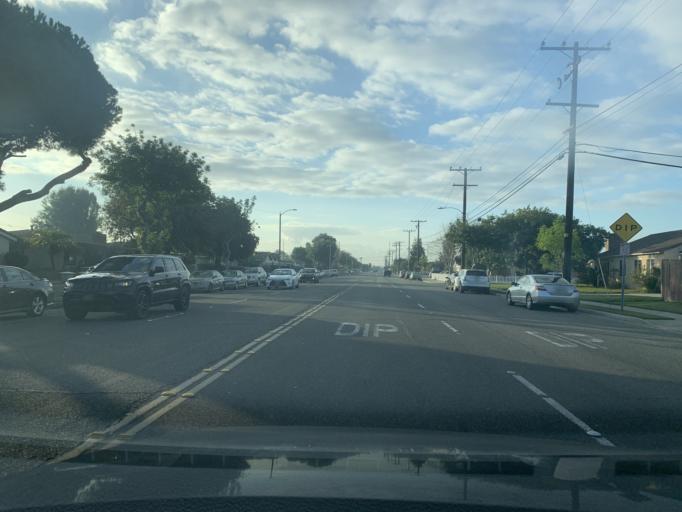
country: US
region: California
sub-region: Orange County
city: Westminster
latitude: 33.7727
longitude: -118.0162
